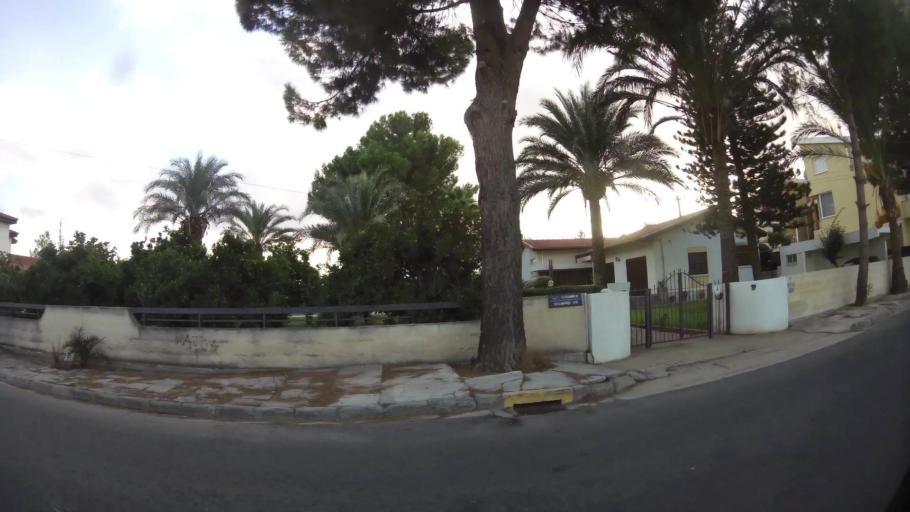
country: CY
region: Lefkosia
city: Tseri
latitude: 35.1222
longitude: 33.3140
